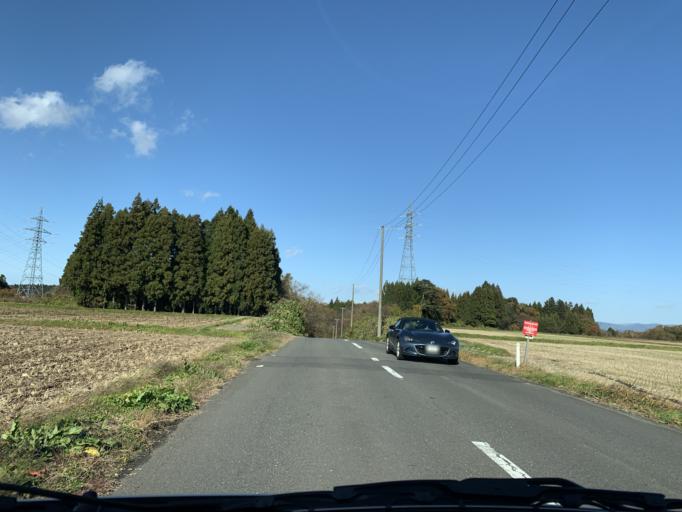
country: JP
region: Iwate
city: Mizusawa
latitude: 39.0878
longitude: 141.1255
